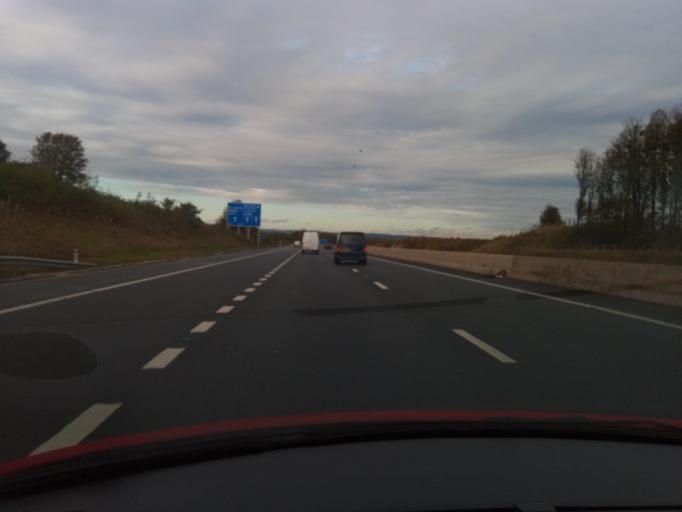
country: GB
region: England
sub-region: Darlington
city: High Coniscliffe
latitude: 54.4575
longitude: -1.6689
